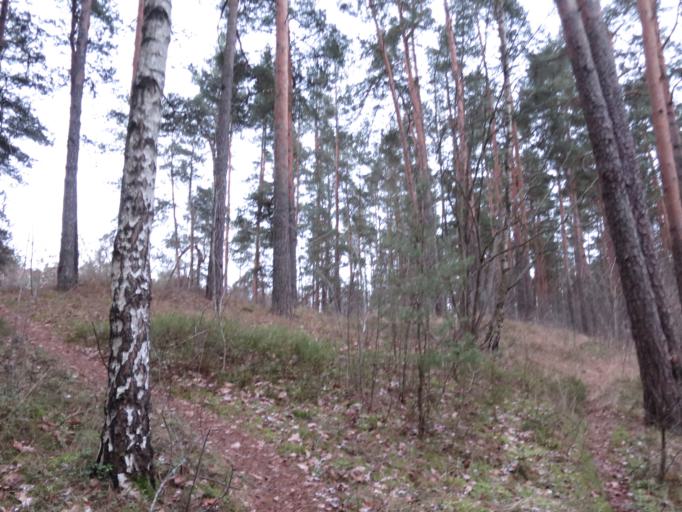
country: LV
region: Riga
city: Bergi
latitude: 56.9772
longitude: 24.3122
